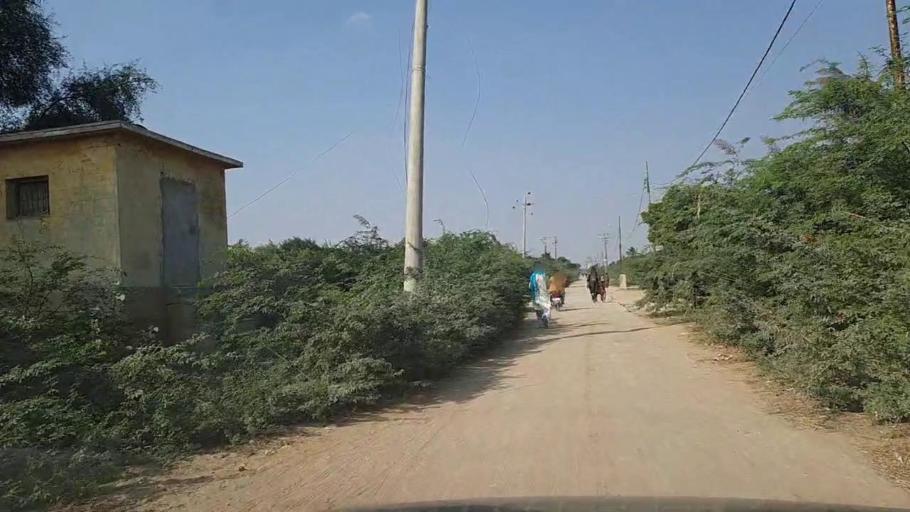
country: PK
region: Sindh
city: Gharo
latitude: 24.7486
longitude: 67.5821
